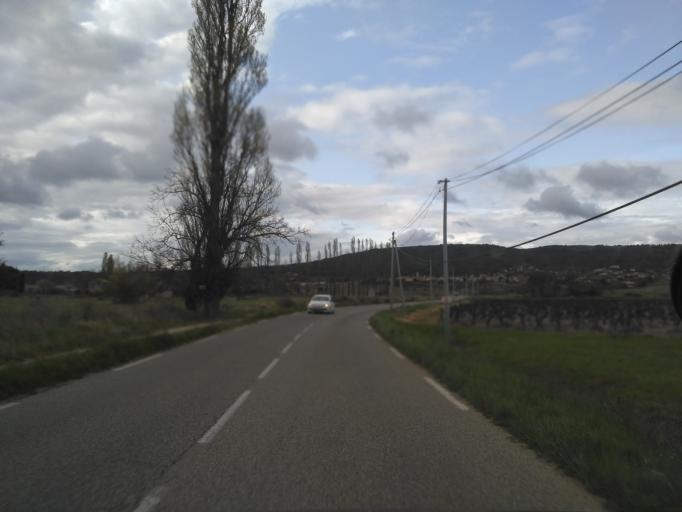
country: FR
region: Provence-Alpes-Cote d'Azur
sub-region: Departement du Var
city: Barjols
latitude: 43.5799
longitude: 6.0154
